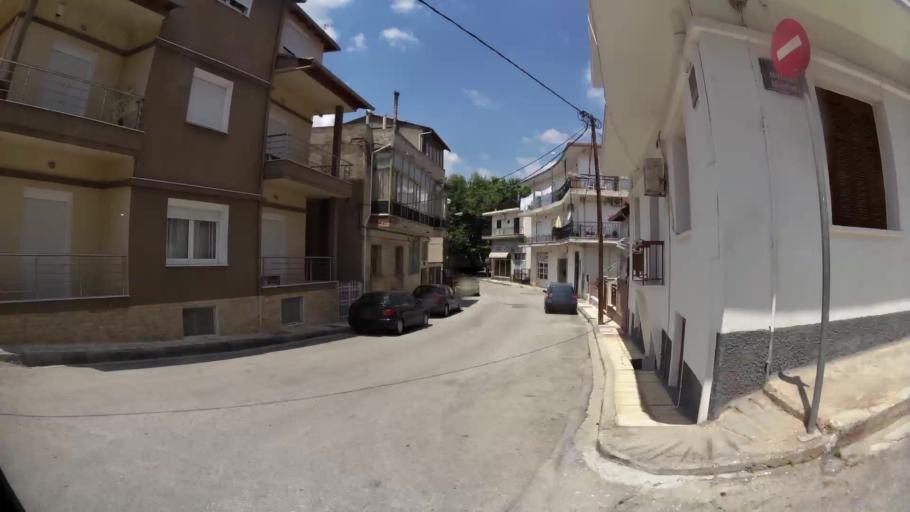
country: GR
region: West Macedonia
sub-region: Nomos Kozanis
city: Kozani
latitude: 40.2955
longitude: 21.7951
